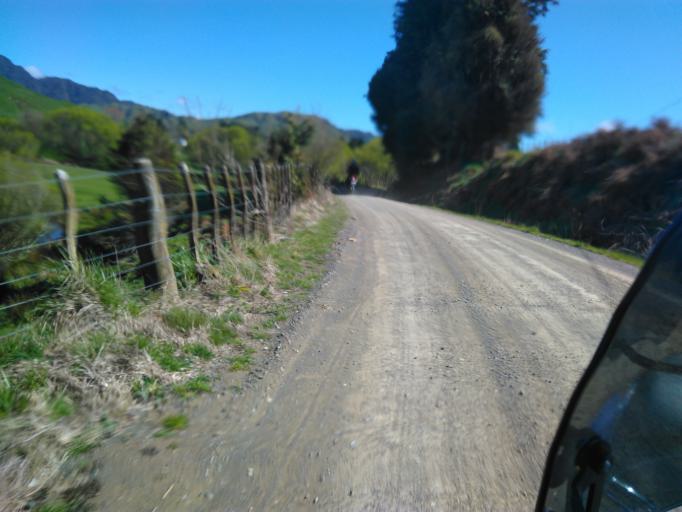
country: NZ
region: Bay of Plenty
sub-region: Opotiki District
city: Opotiki
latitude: -38.2873
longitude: 177.5440
